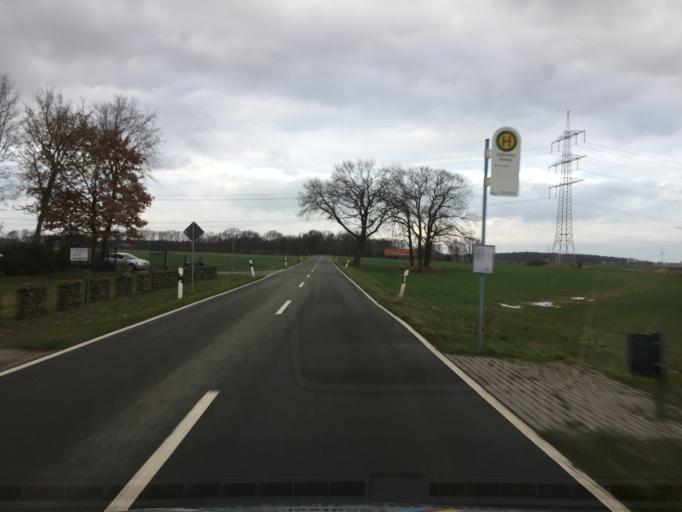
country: DE
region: Lower Saxony
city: Steyerberg
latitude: 52.5439
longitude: 9.0278
